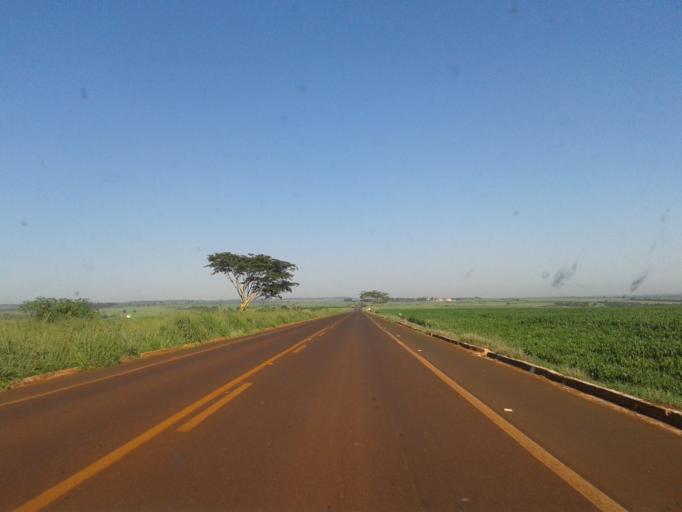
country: BR
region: Minas Gerais
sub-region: Capinopolis
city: Capinopolis
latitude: -18.6992
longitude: -49.6471
